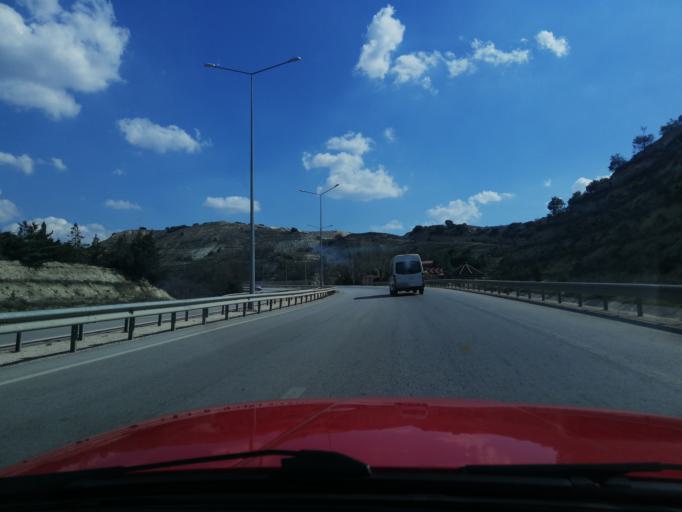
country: TR
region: Burdur
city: Burdur
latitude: 37.7035
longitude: 30.3068
